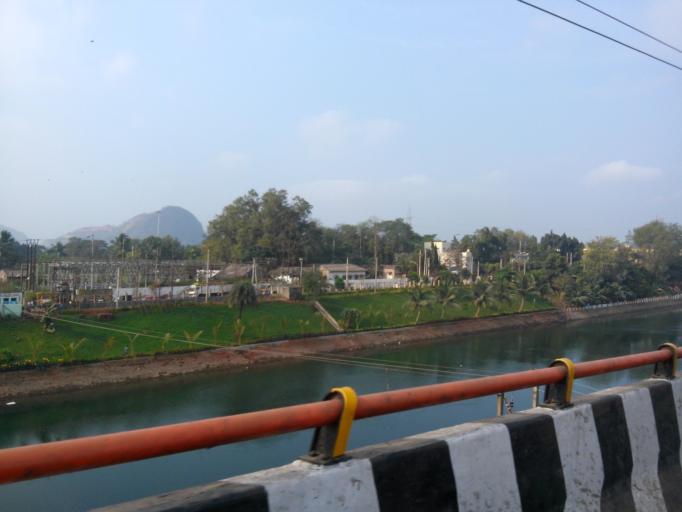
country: IN
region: Andhra Pradesh
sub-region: Krishna
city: Vijayawada
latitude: 16.5117
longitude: 80.6139
